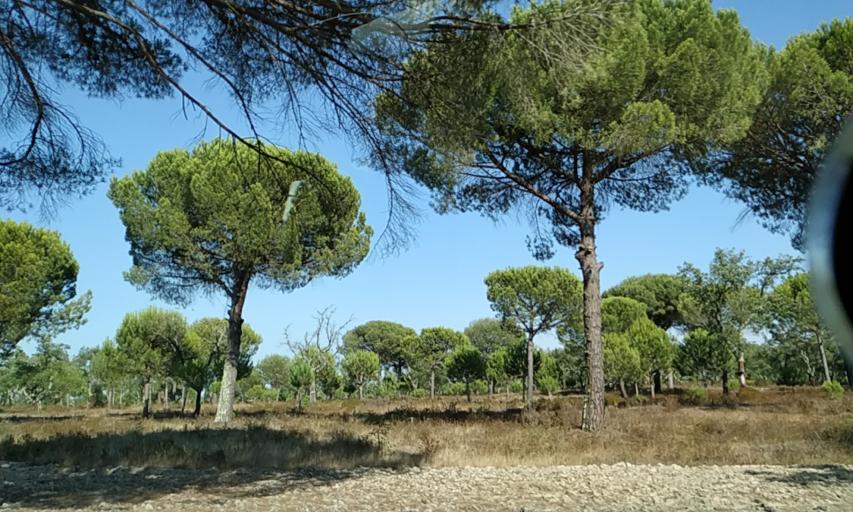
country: PT
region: Santarem
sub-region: Coruche
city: Coruche
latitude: 38.8376
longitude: -8.5577
